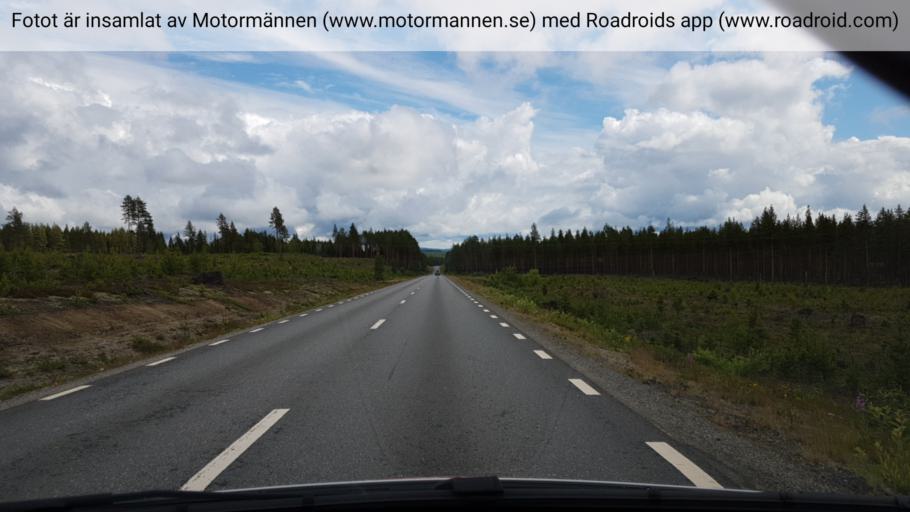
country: SE
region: Vaesterbotten
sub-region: Lycksele Kommun
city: Lycksele
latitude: 64.3918
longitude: 19.0814
